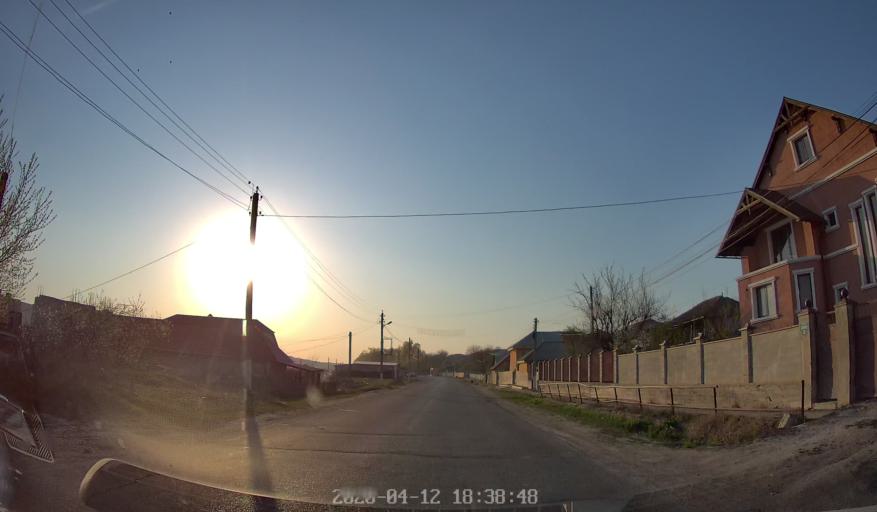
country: MD
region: Chisinau
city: Vadul lui Voda
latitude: 47.1258
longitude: 28.9960
